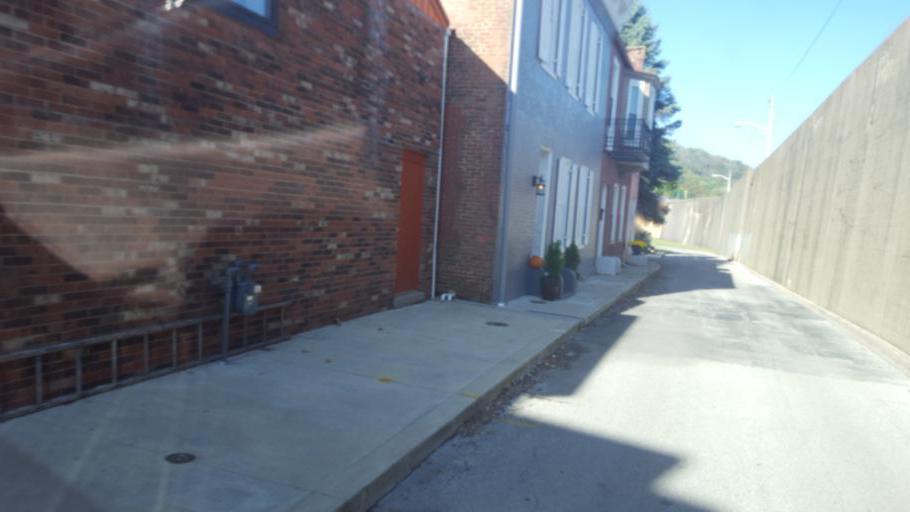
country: US
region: Ohio
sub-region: Brown County
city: Aberdeen
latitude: 38.6496
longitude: -83.7662
